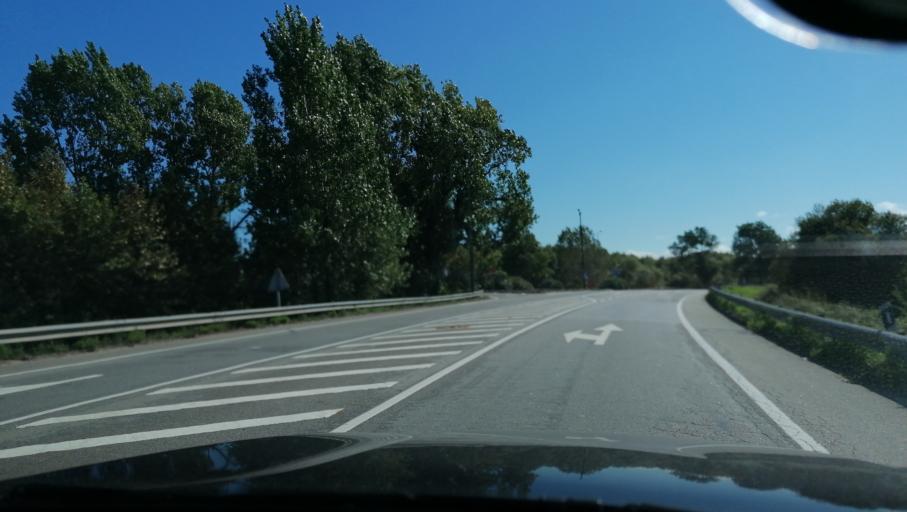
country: PT
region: Aveiro
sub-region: Estarreja
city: Salreu
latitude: 40.6864
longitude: -8.5582
